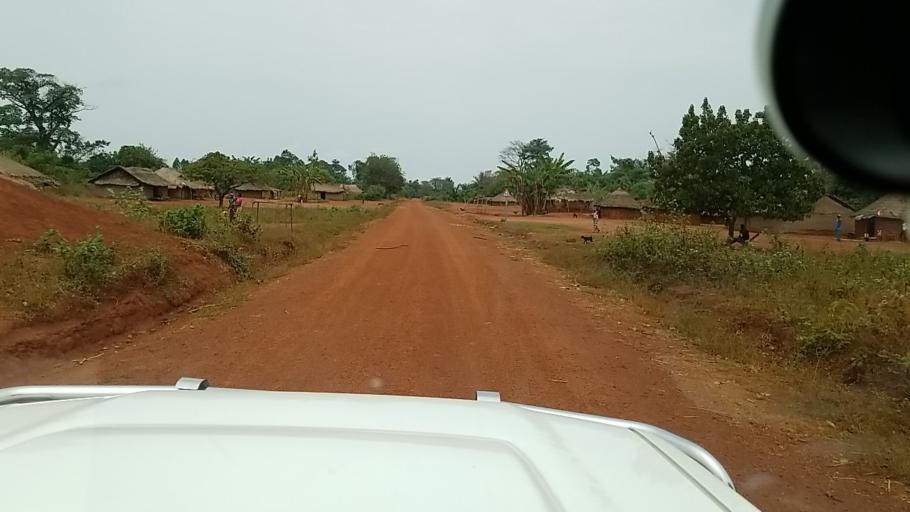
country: CD
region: Equateur
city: Gemena
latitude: 3.5197
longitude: 19.3673
